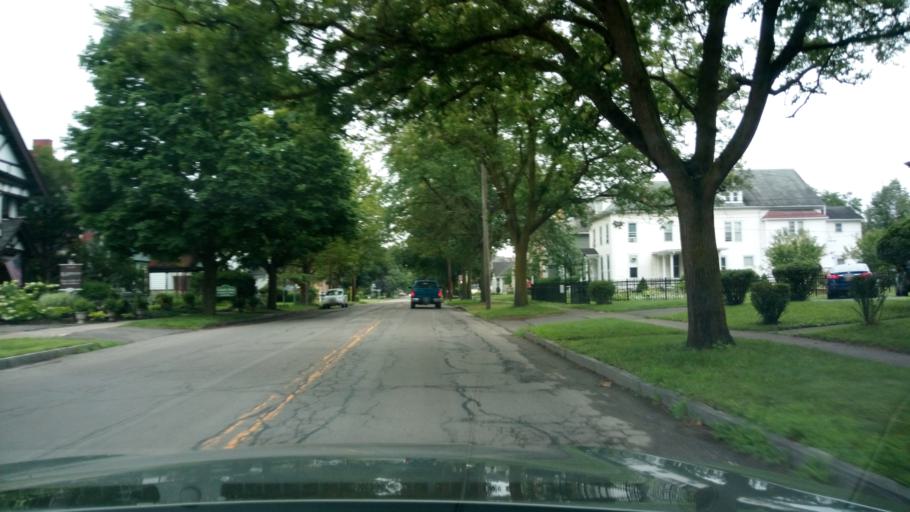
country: US
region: New York
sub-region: Chemung County
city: Elmira
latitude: 42.0887
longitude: -76.8126
